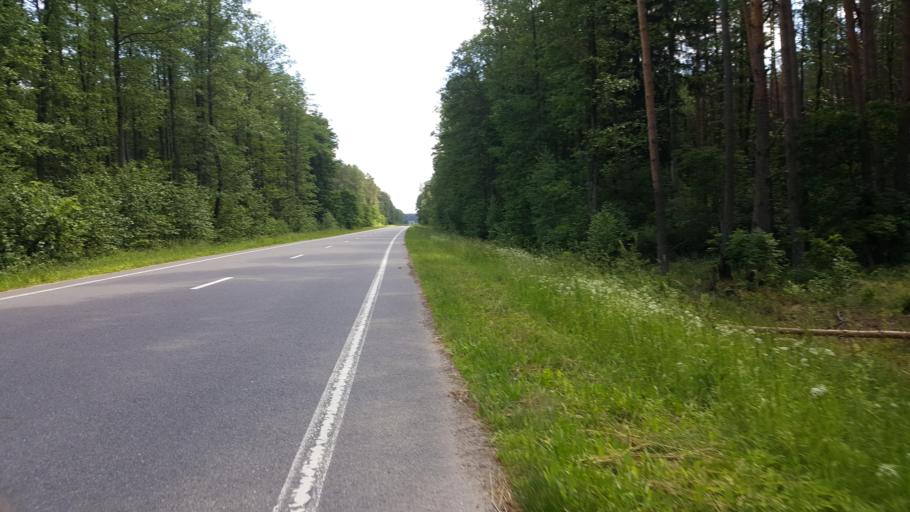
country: BY
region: Brest
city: Kamyanyuki
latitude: 52.5388
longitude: 23.6542
